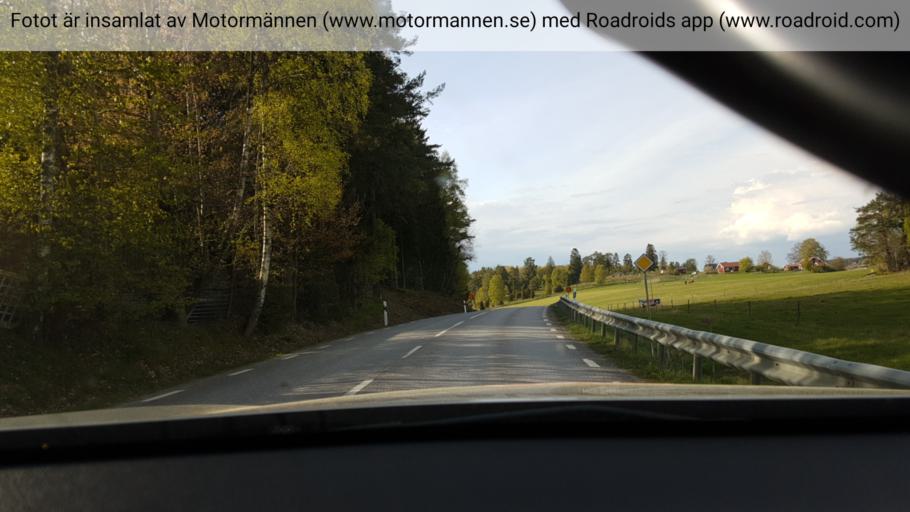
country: SE
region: Stockholm
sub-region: Nynashamns Kommun
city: Osmo
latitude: 58.9916
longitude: 17.8114
